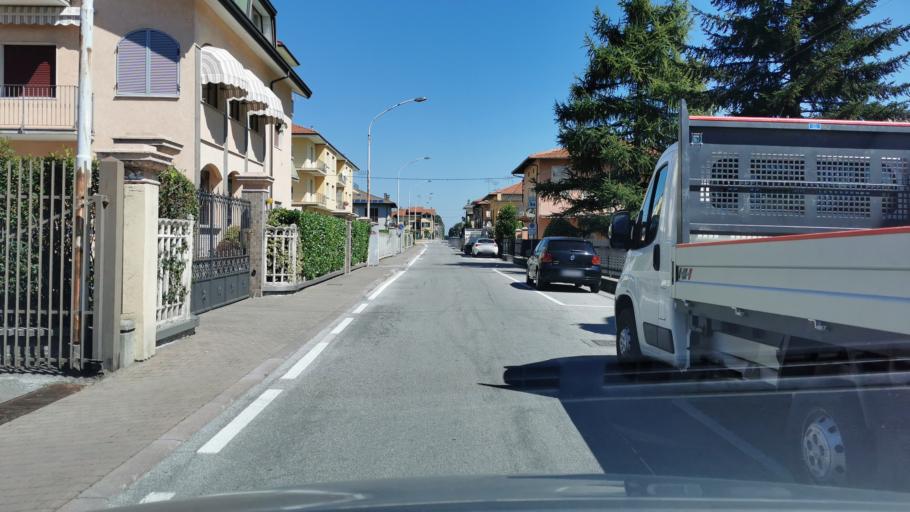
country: IT
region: Piedmont
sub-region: Provincia di Cuneo
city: Borgo San Dalmazzo
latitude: 44.3313
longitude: 7.4844
